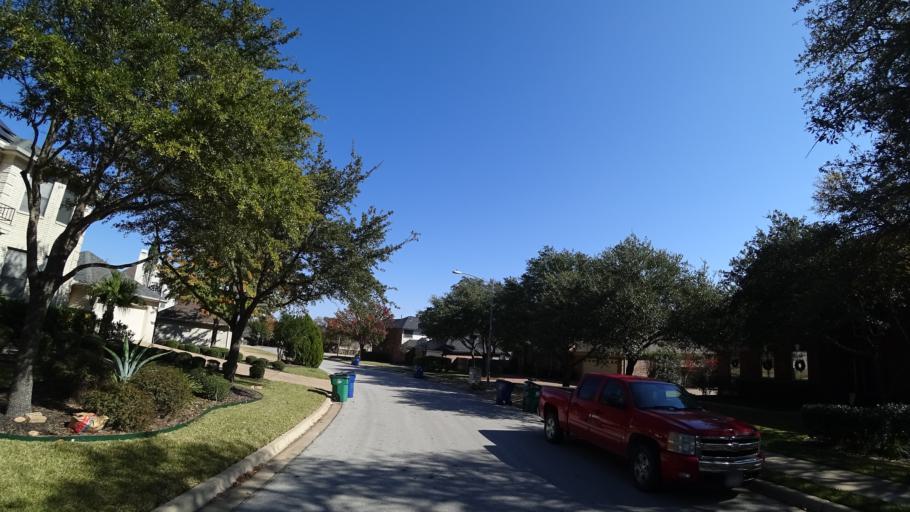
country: US
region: Texas
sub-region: Travis County
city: Lost Creek
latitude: 30.3747
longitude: -97.8466
